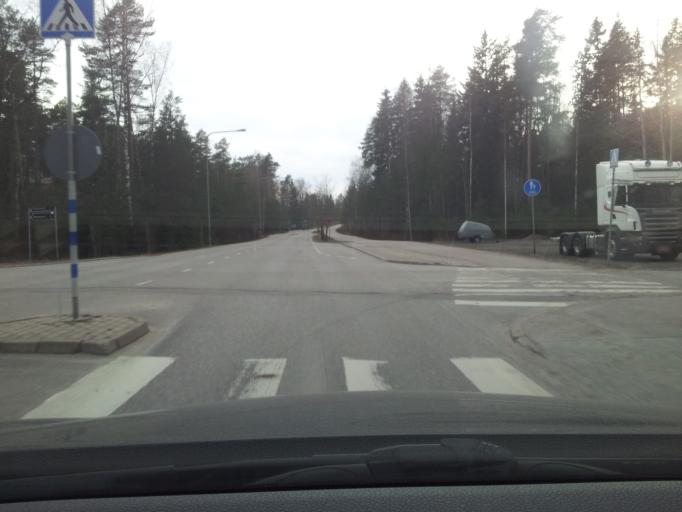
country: FI
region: Uusimaa
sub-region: Helsinki
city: Espoo
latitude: 60.1667
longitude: 24.6895
